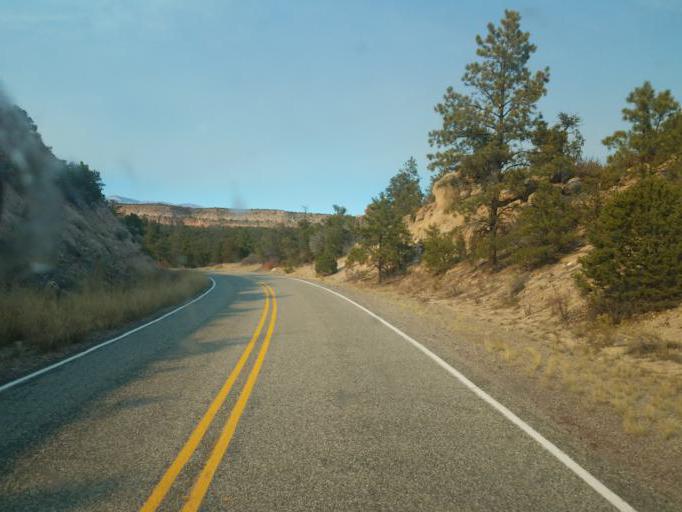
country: US
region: New Mexico
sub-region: Los Alamos County
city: White Rock
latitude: 35.8026
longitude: -106.2452
